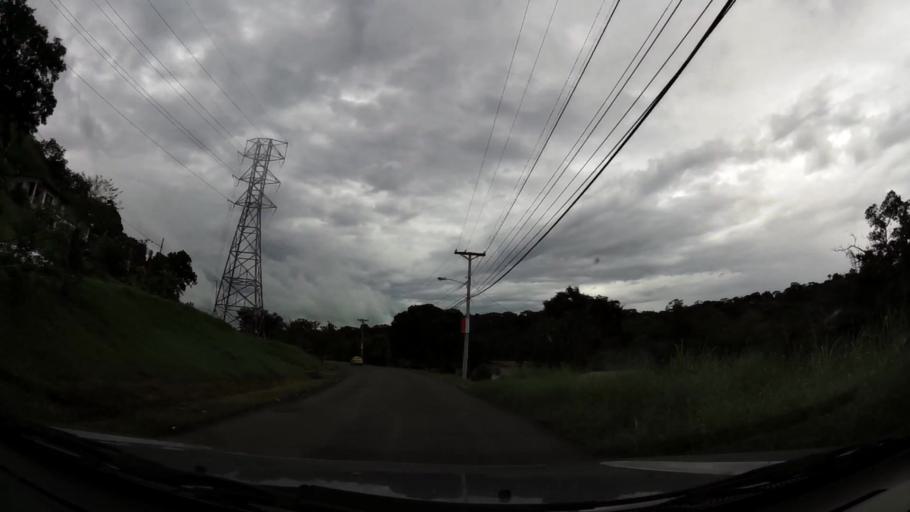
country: PA
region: Panama
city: Chilibre
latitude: 9.1674
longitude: -79.6132
